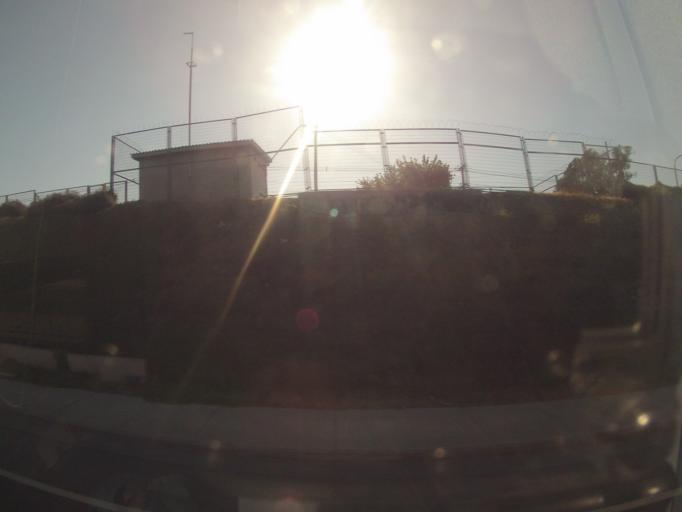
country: CL
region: Santiago Metropolitan
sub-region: Provincia de Maipo
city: San Bernardo
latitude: -33.6384
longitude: -70.7125
